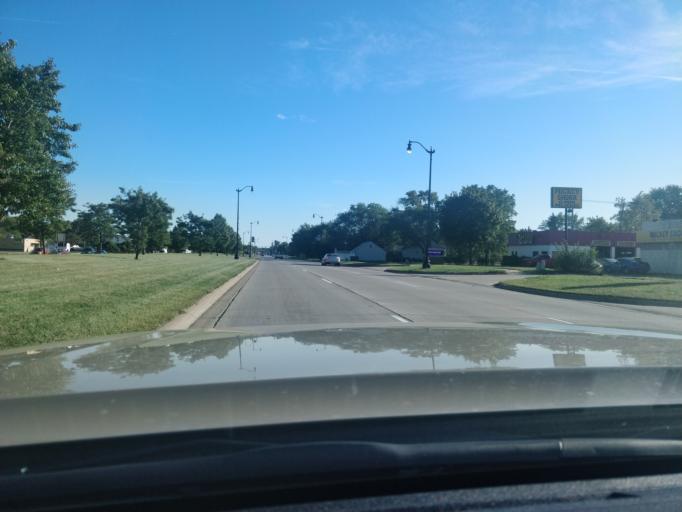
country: US
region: Michigan
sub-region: Wayne County
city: Taylor
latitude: 42.2031
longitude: -83.2685
